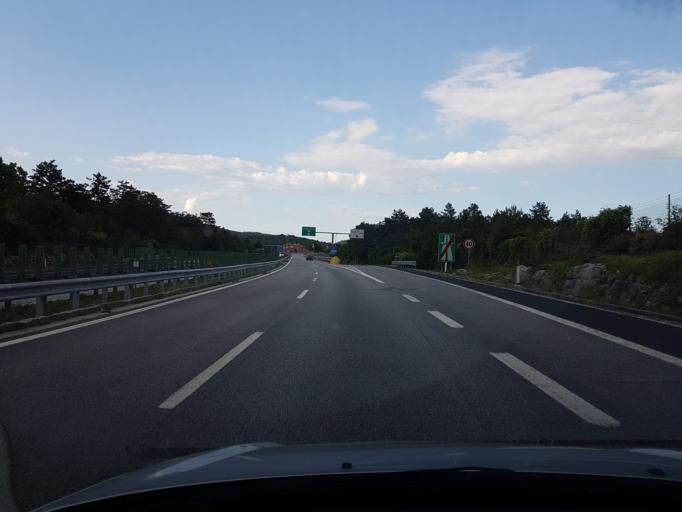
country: IT
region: Friuli Venezia Giulia
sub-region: Provincia di Trieste
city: Zolla
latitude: 45.6954
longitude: 13.8311
